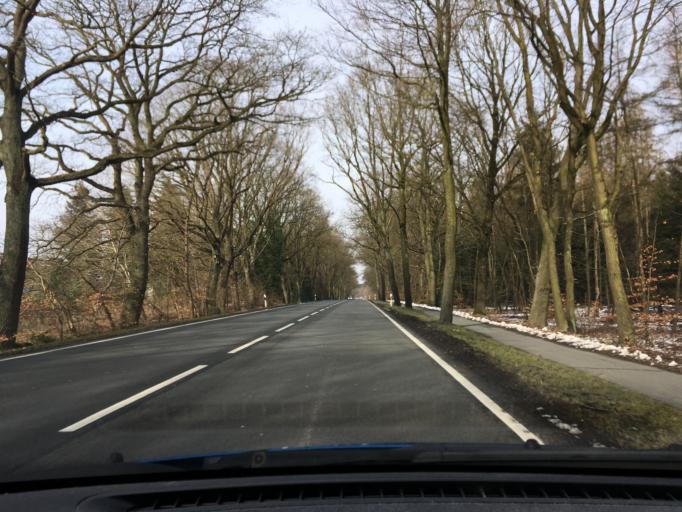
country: DE
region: Lower Saxony
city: Barendorf
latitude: 53.2260
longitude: 10.5464
